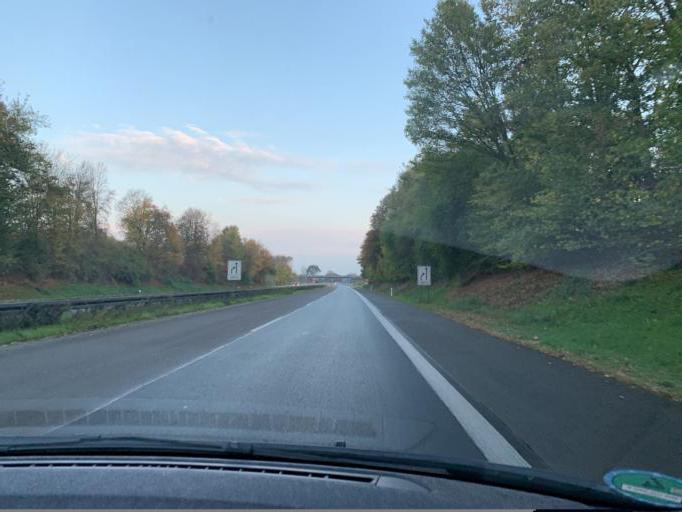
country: DE
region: North Rhine-Westphalia
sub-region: Regierungsbezirk Dusseldorf
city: Juchen
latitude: 51.1085
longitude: 6.4766
